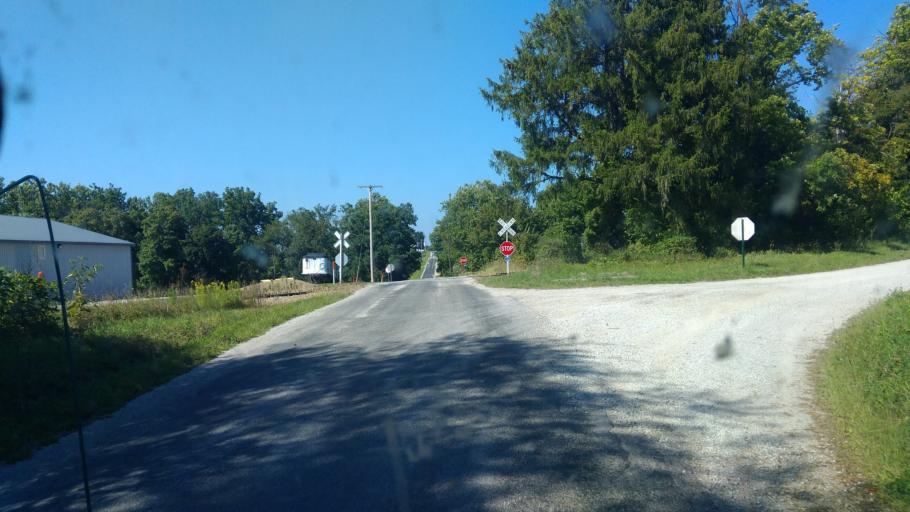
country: US
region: Ohio
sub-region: Ashland County
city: Ashland
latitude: 40.9218
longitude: -82.2625
